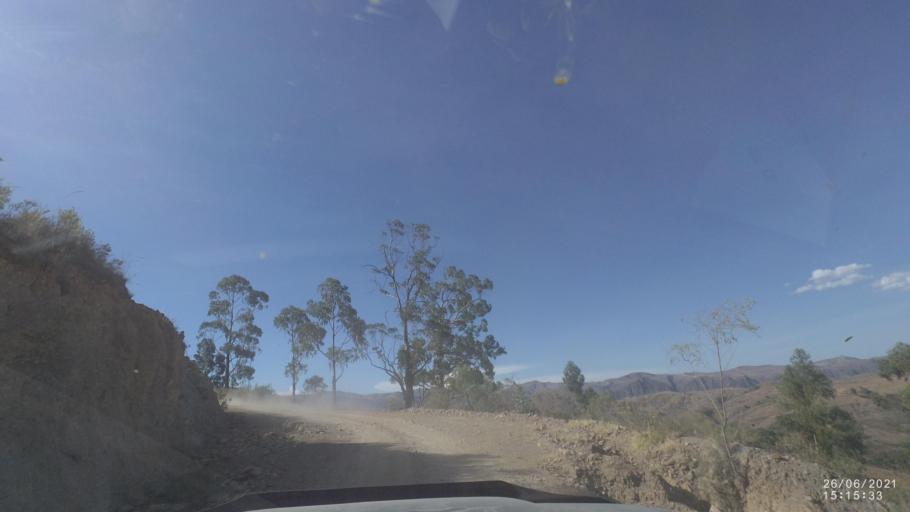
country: BO
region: Cochabamba
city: Mizque
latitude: -17.9583
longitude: -65.6464
